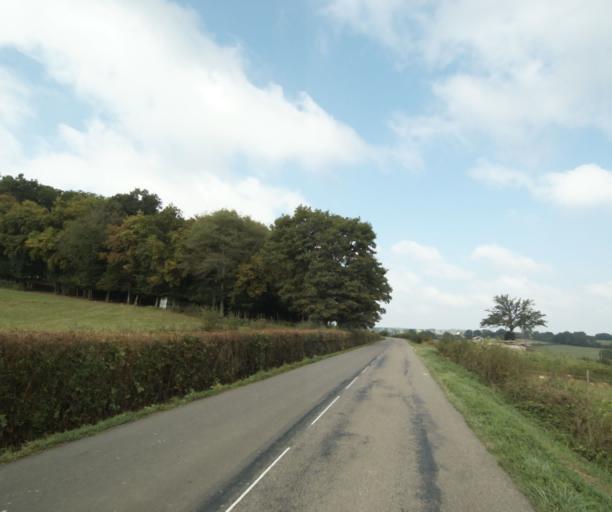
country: FR
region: Bourgogne
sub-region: Departement de Saone-et-Loire
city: Charolles
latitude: 46.4268
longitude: 4.3060
